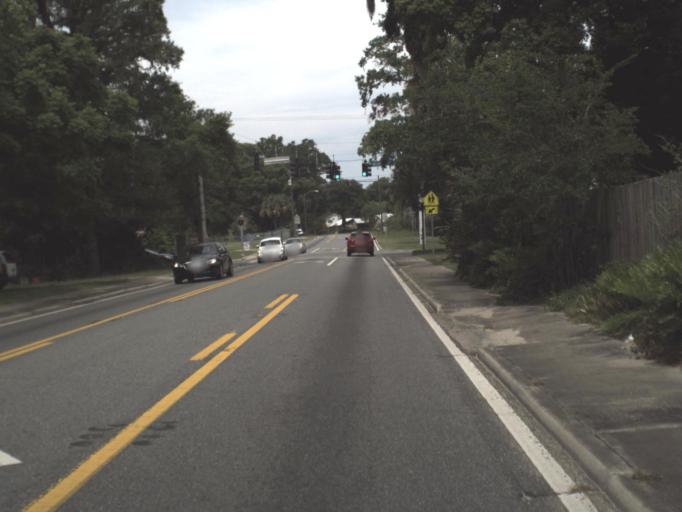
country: US
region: Florida
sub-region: Putnam County
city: Palatka
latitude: 29.6434
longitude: -81.6489
